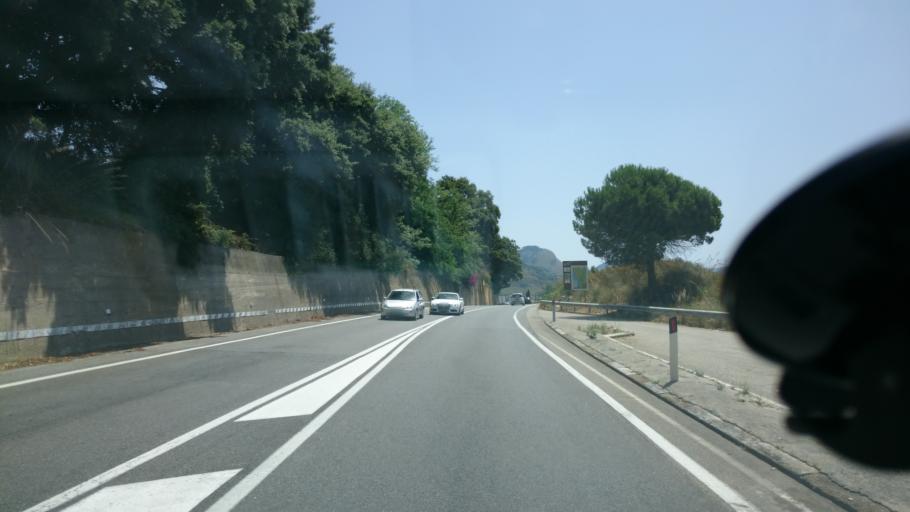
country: IT
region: Calabria
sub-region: Provincia di Cosenza
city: Cittadella del Capo
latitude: 39.5393
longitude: 15.8986
